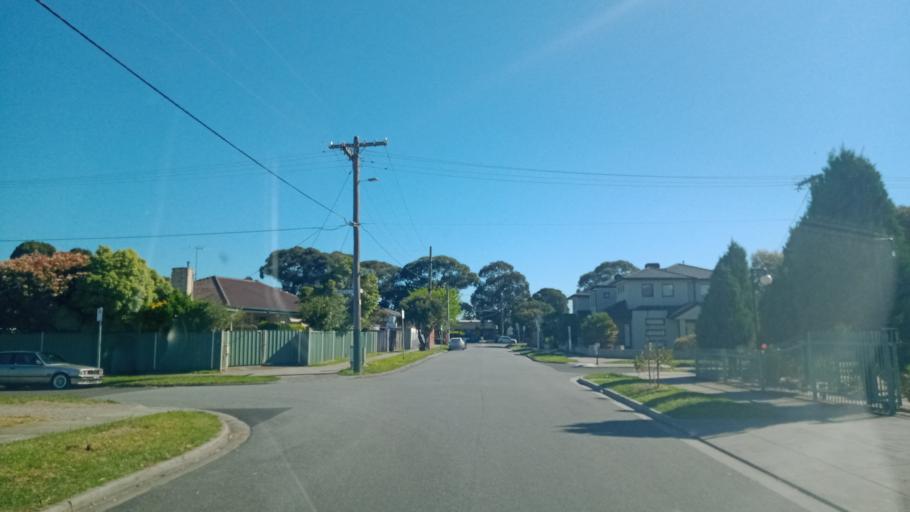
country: AU
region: Victoria
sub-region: Greater Dandenong
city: Springvale
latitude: -37.9358
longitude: 145.1691
